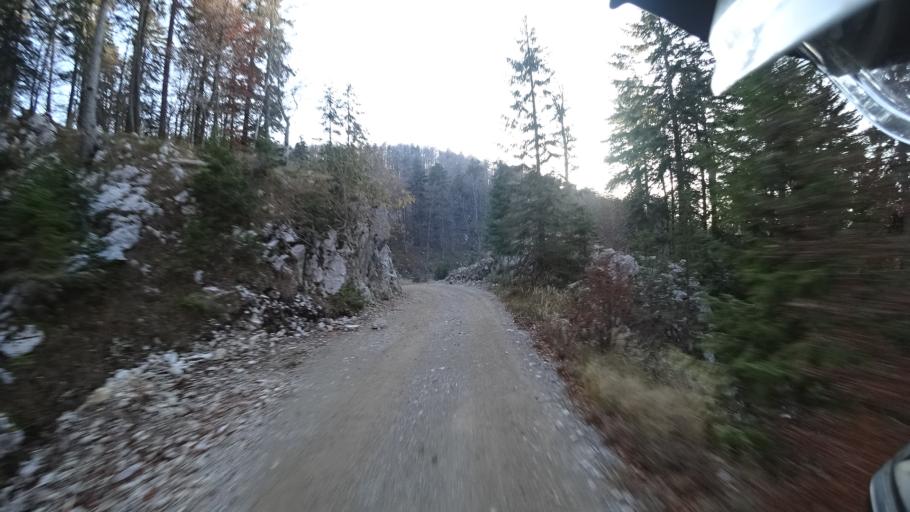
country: HR
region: Primorsko-Goranska
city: Drazice
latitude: 45.4872
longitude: 14.4885
